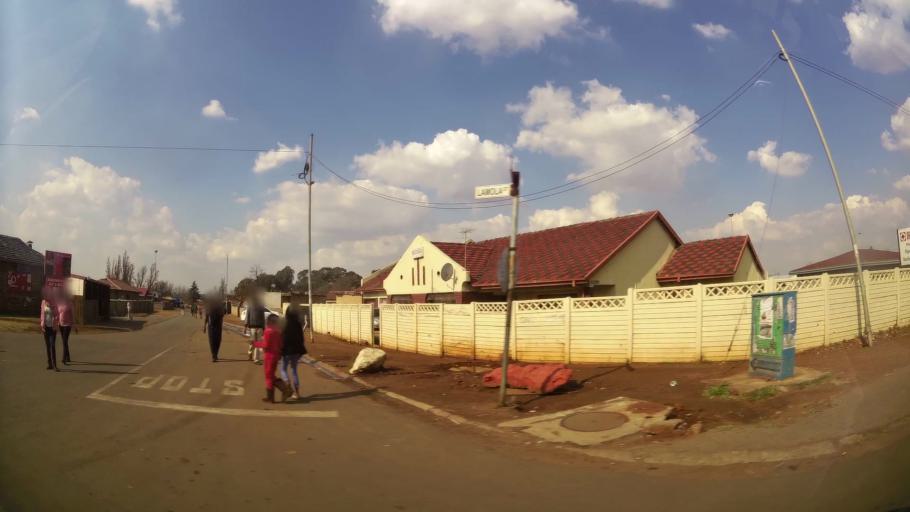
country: ZA
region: Gauteng
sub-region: Ekurhuleni Metropolitan Municipality
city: Germiston
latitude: -26.3090
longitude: 28.1578
